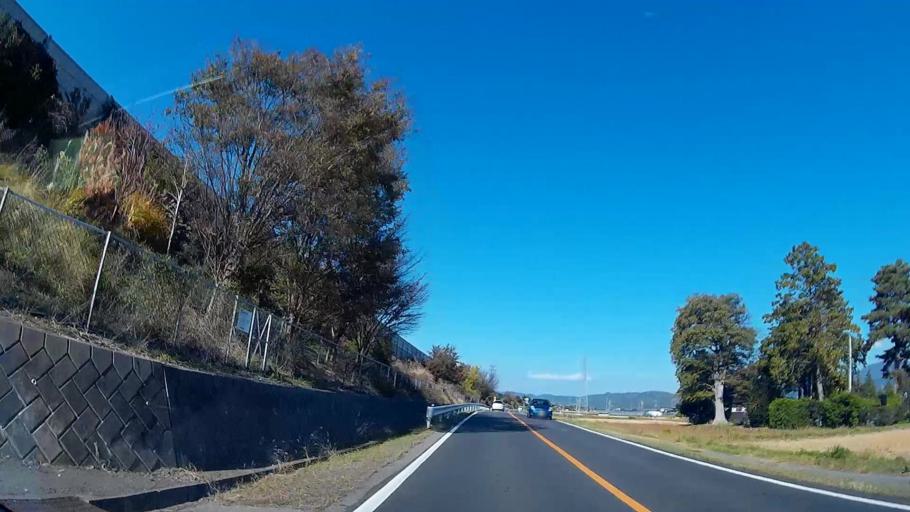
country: JP
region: Nagano
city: Matsumoto
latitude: 36.2105
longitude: 137.9299
